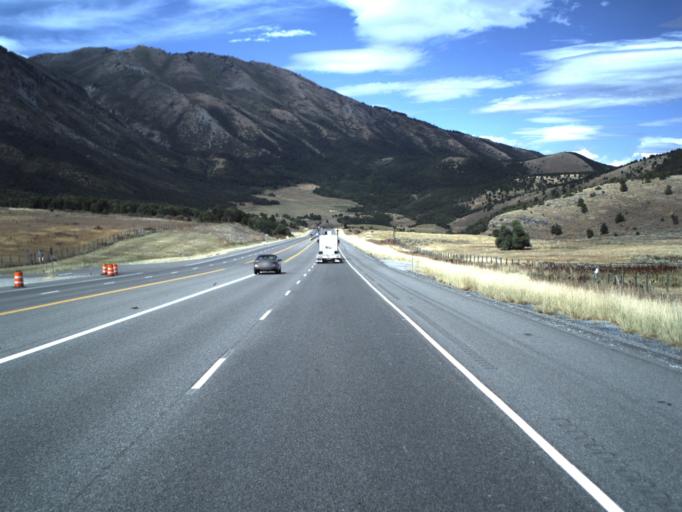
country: US
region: Utah
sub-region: Cache County
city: Wellsville
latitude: 41.5837
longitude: -111.9749
